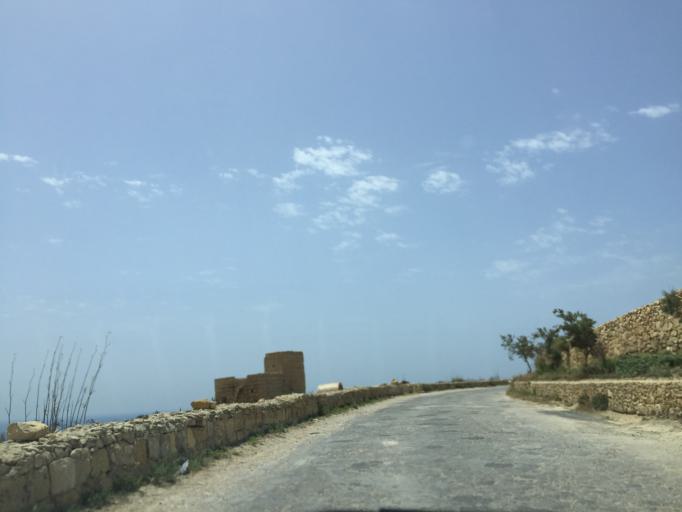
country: MT
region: Saint Lucia
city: Saint Lucia
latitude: 36.0357
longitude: 14.2060
